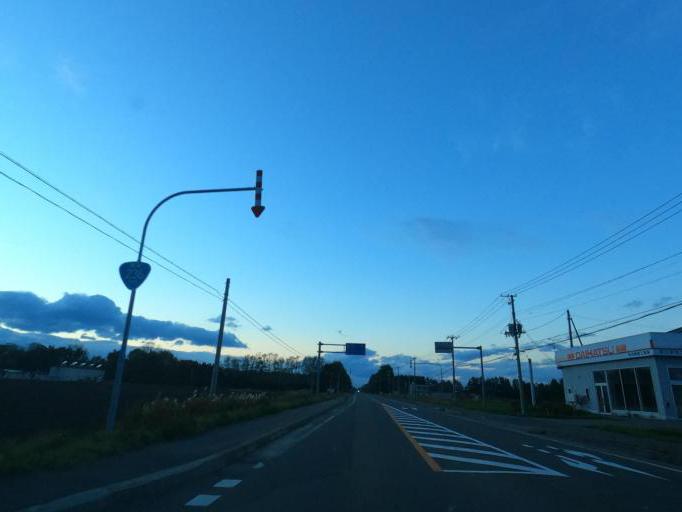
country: JP
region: Hokkaido
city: Obihiro
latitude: 42.6543
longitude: 143.1887
